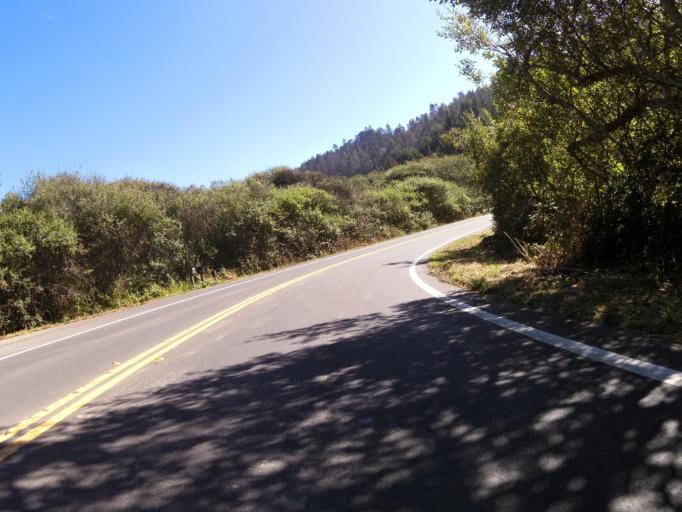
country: US
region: California
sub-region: Mendocino County
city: Fort Bragg
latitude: 39.6497
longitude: -123.7800
